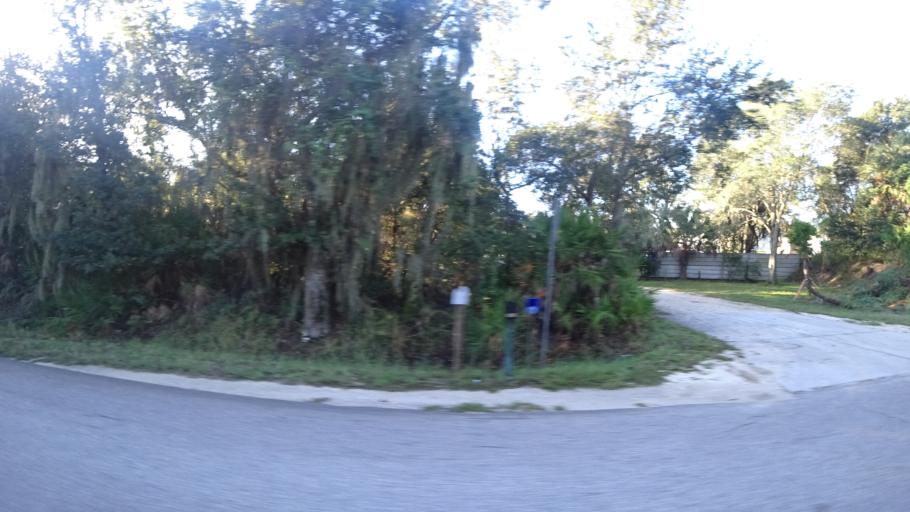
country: US
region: Florida
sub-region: Manatee County
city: Ellenton
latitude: 27.5469
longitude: -82.5319
